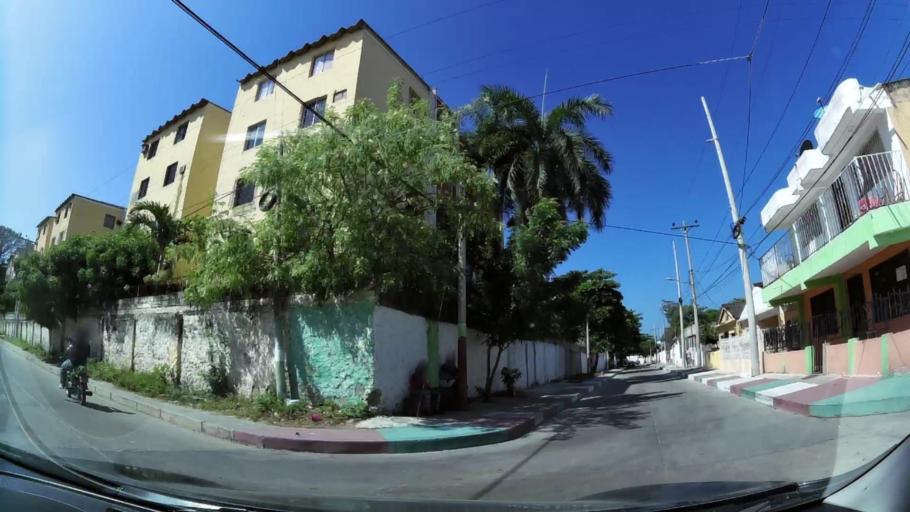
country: CO
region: Bolivar
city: Cartagena
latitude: 10.4395
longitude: -75.5173
